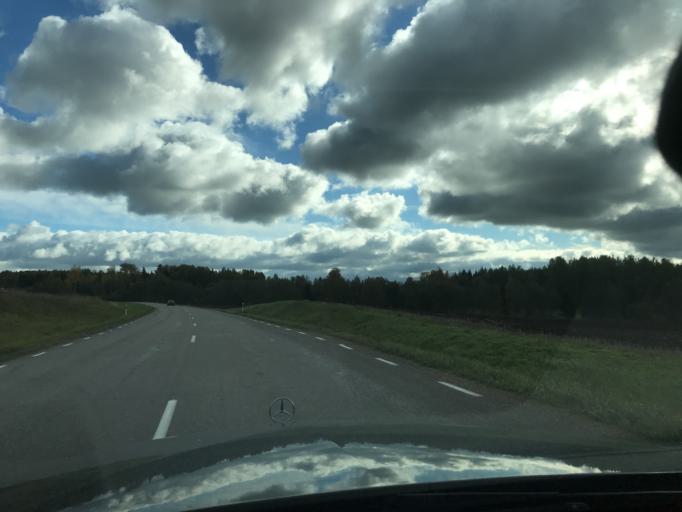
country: EE
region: Vorumaa
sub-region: Antsla vald
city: Vana-Antsla
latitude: 57.9060
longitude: 26.4246
